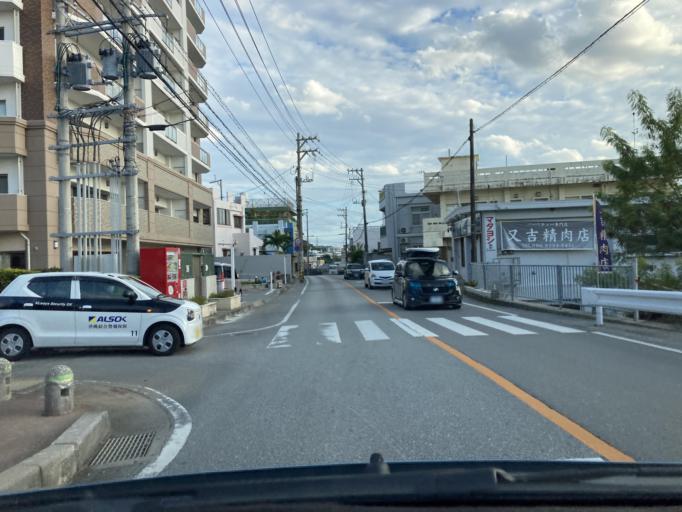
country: JP
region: Okinawa
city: Chatan
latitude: 26.3168
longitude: 127.7719
